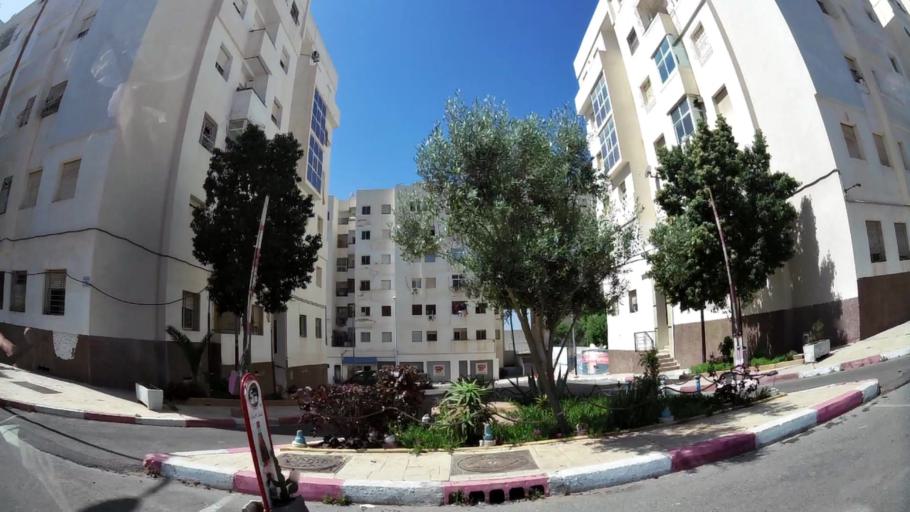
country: MA
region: Oued ed Dahab-Lagouira
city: Dakhla
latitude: 30.4348
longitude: -9.5666
